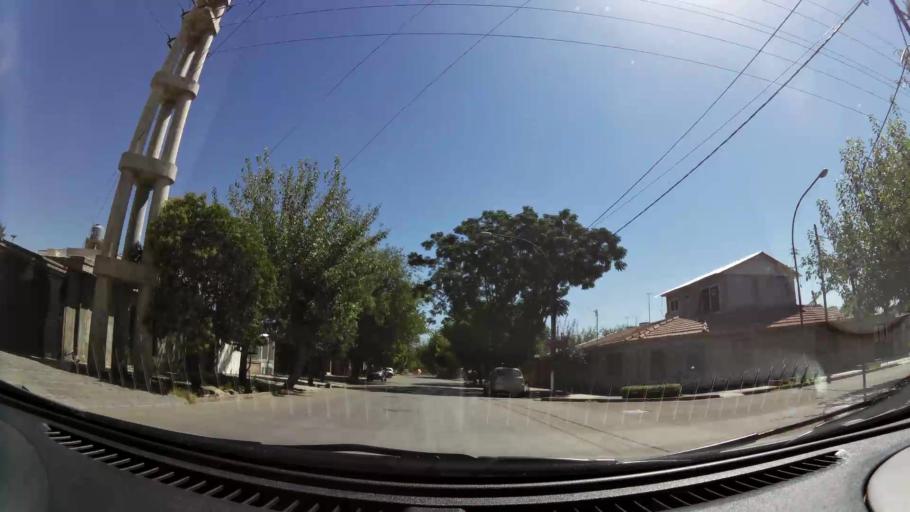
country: AR
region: Mendoza
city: Mendoza
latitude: -32.8788
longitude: -68.8072
